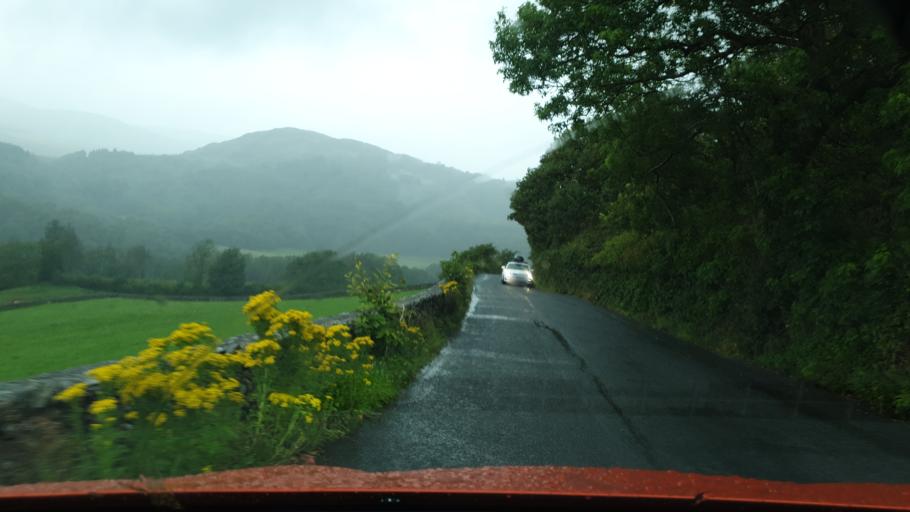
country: GB
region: England
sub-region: Cumbria
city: Millom
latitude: 54.2953
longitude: -3.2289
